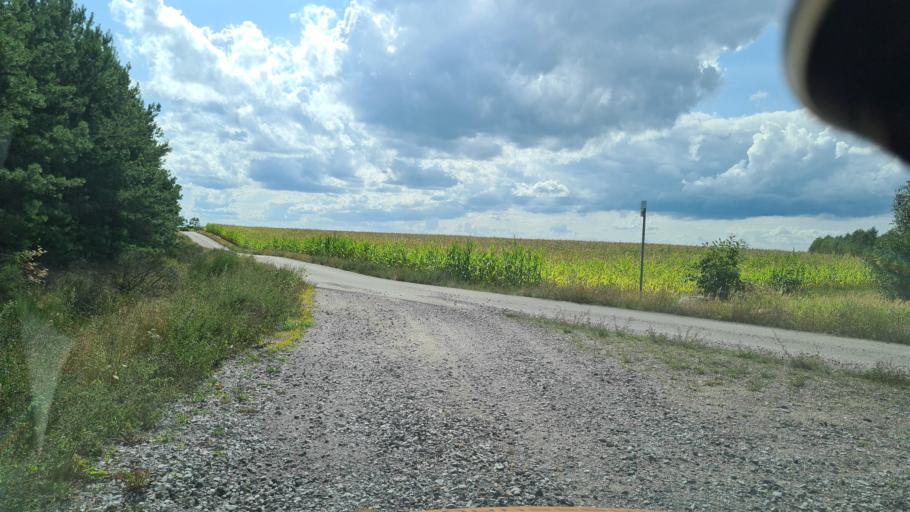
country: DE
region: Brandenburg
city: Drebkau
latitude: 51.6035
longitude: 14.2919
